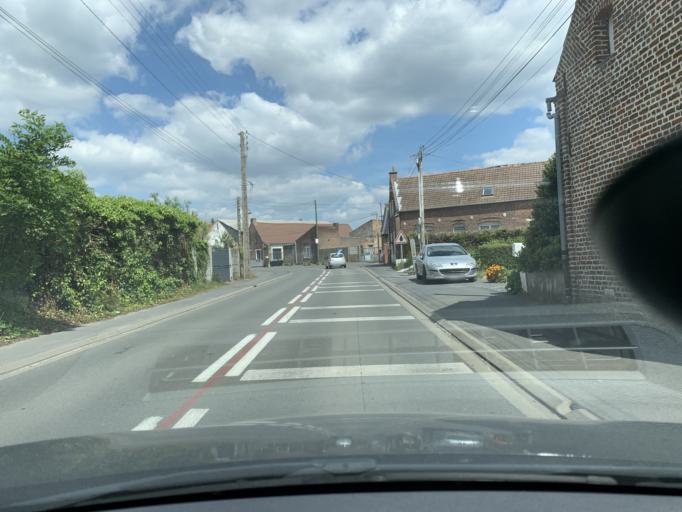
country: FR
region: Nord-Pas-de-Calais
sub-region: Departement du Nord
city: Goeulzin
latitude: 50.3173
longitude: 3.0973
